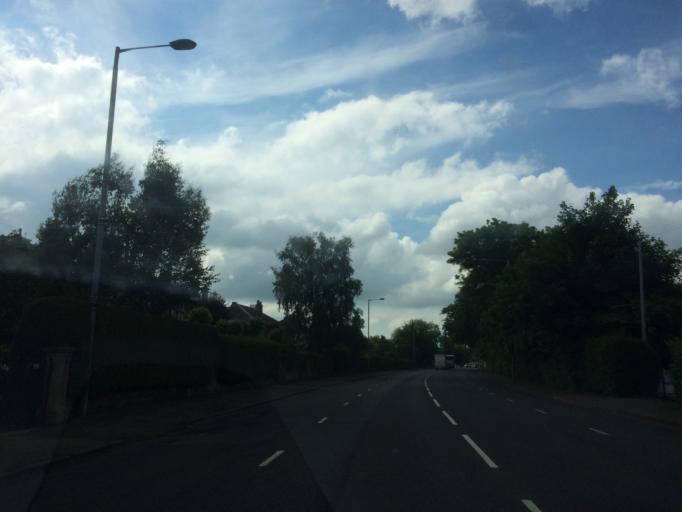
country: GB
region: Scotland
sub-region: East Renfrewshire
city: Giffnock
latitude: 55.8331
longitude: -4.2960
